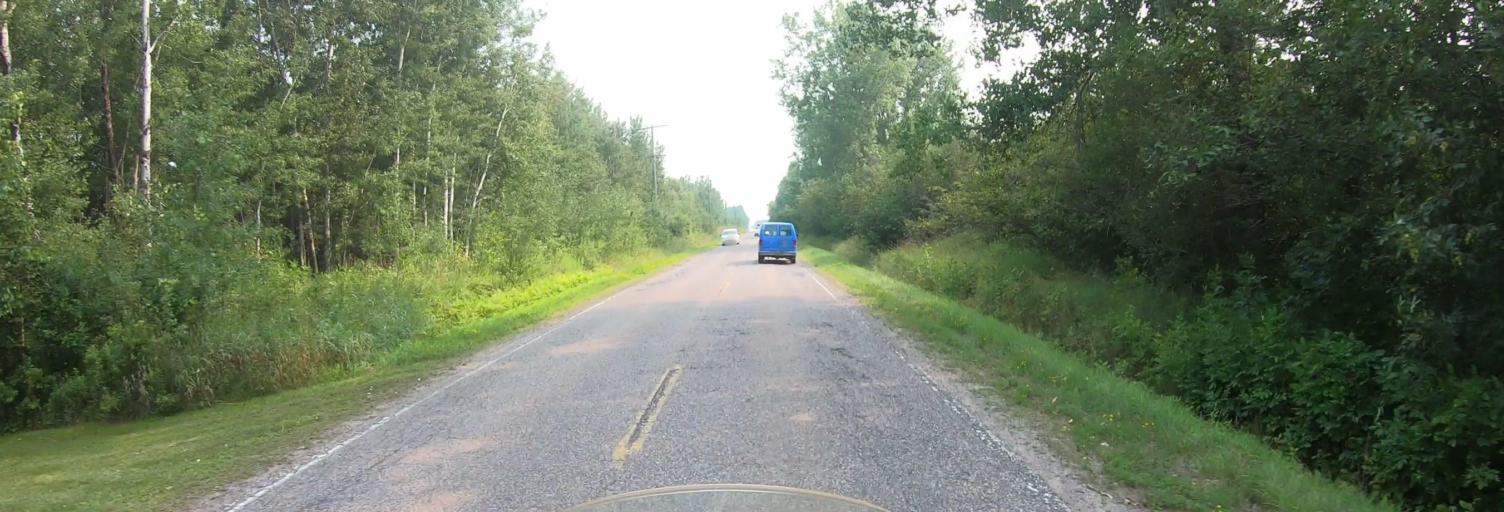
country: US
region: Michigan
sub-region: Chippewa County
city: Sault Ste. Marie
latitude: 46.4669
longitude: -84.3014
